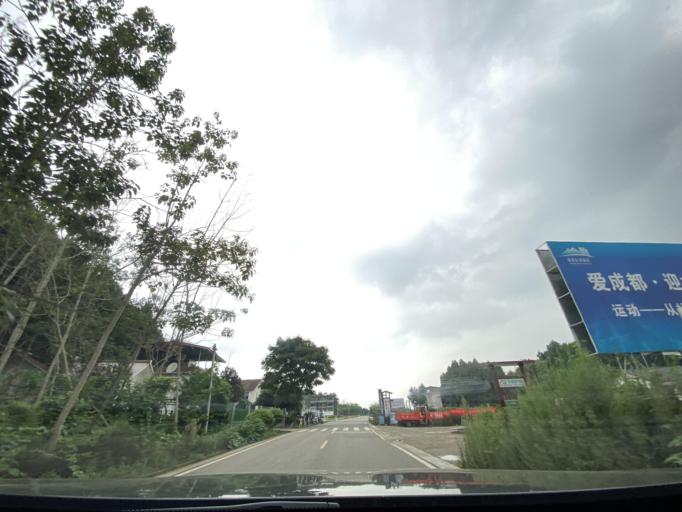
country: CN
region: Sichuan
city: Jiancheng
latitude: 30.5337
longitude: 104.5363
